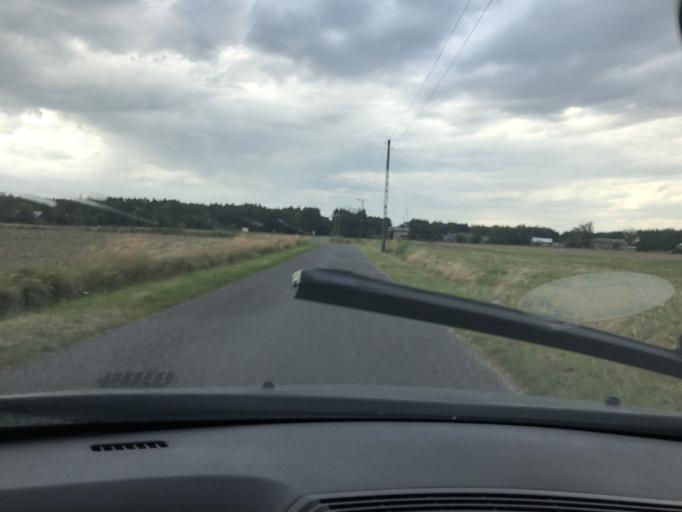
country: PL
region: Lodz Voivodeship
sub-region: Powiat wieruszowski
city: Czastary
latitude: 51.2405
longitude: 18.3005
